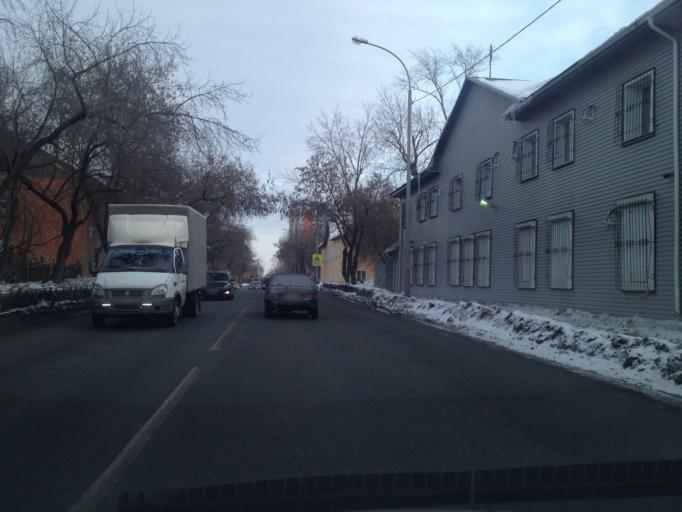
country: RU
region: Sverdlovsk
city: Yekaterinburg
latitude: 56.8647
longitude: 60.5726
